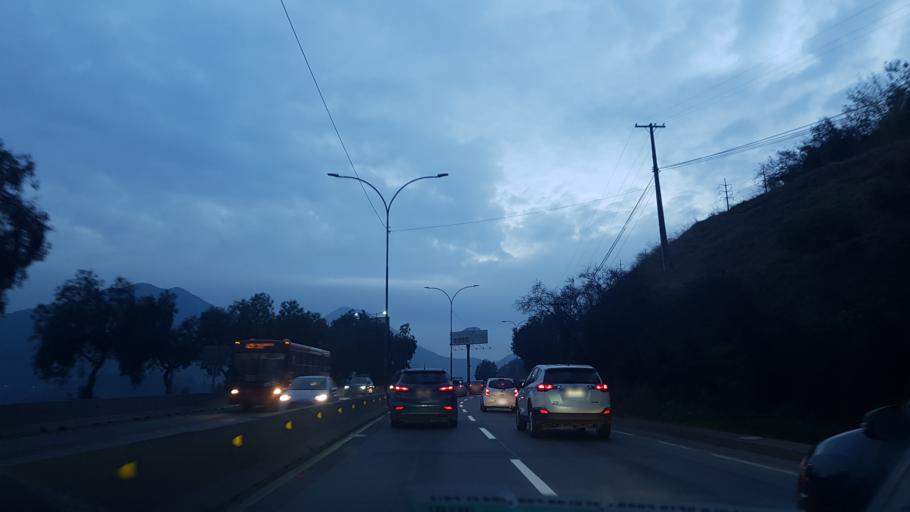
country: CL
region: Santiago Metropolitan
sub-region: Provincia de Santiago
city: Santiago
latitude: -33.3973
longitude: -70.6123
